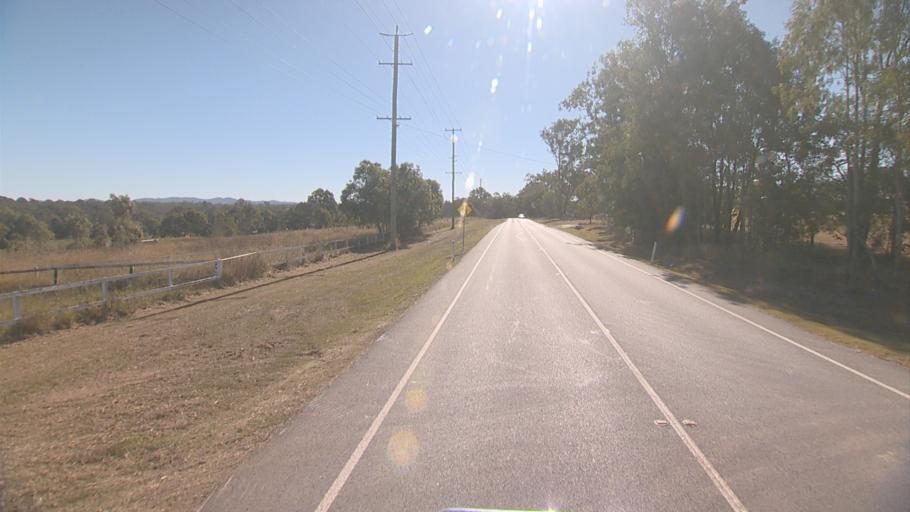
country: AU
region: Queensland
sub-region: Logan
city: North Maclean
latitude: -27.7700
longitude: 153.0029
